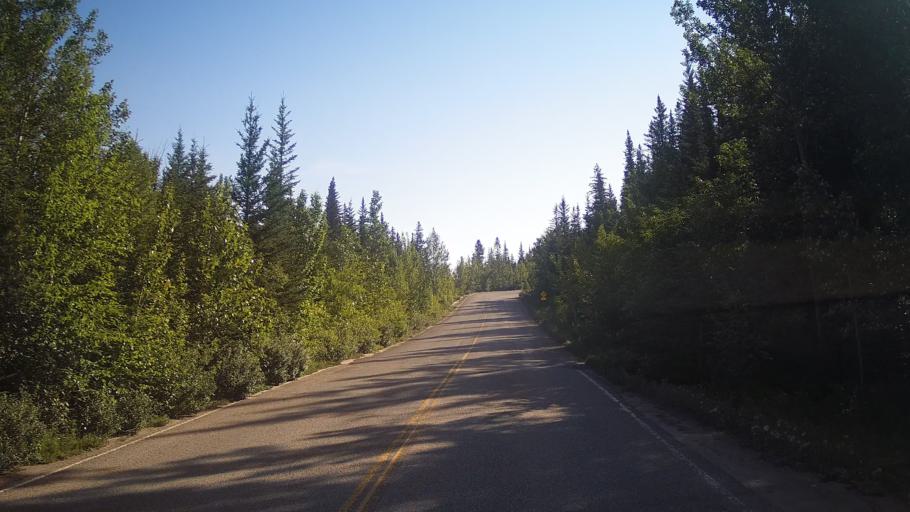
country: CA
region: Alberta
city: Jasper Park Lodge
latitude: 53.2045
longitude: -117.9245
